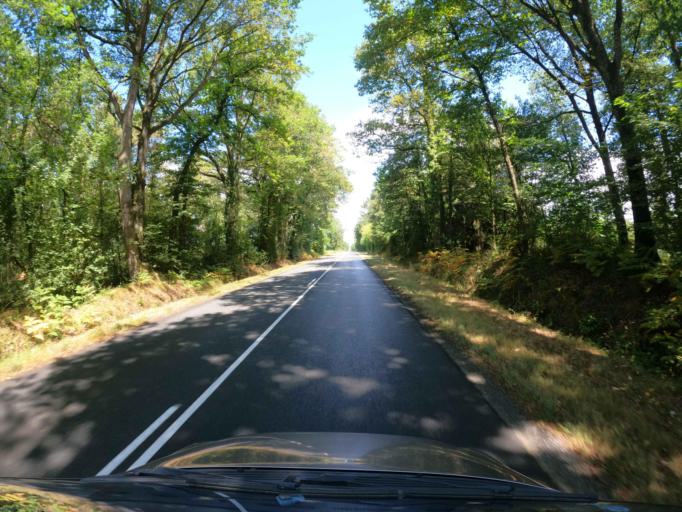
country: FR
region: Pays de la Loire
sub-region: Departement de Maine-et-Loire
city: Champigne
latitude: 47.6223
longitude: -0.5829
